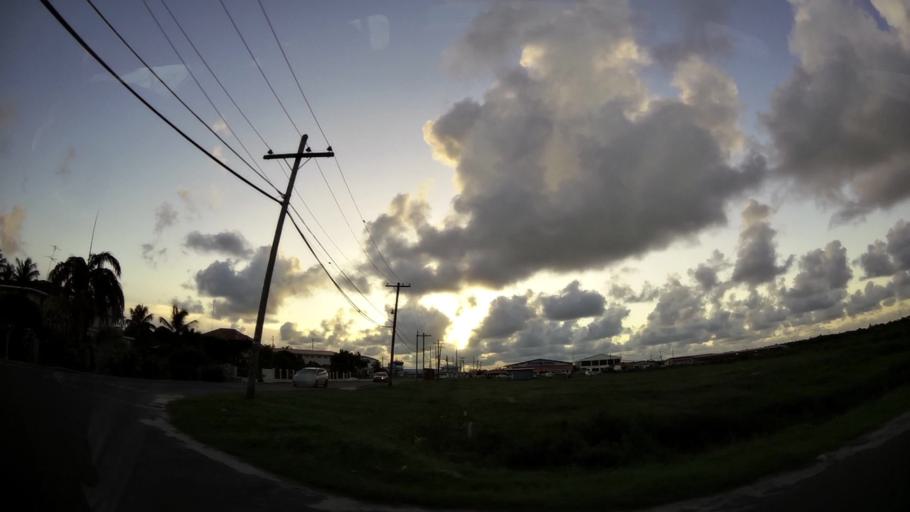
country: GY
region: Demerara-Mahaica
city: Georgetown
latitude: 6.8066
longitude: -58.1012
